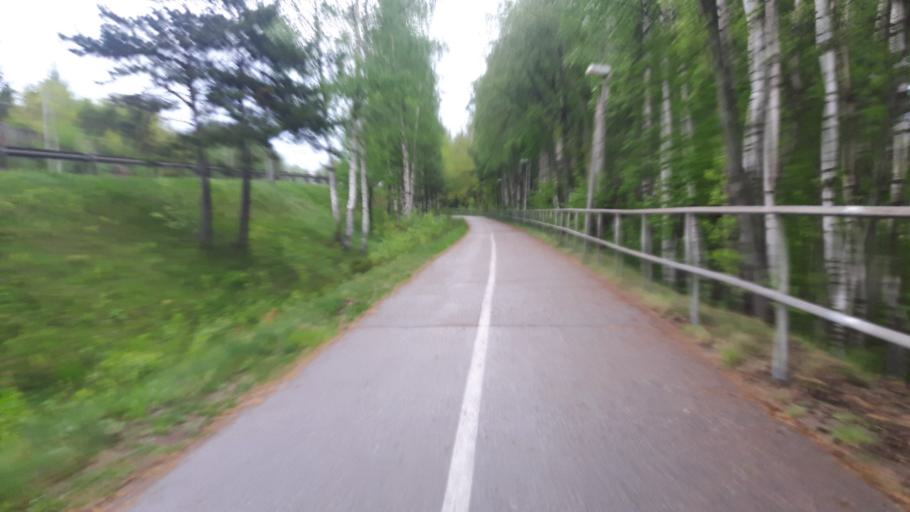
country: FI
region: Kymenlaakso
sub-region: Kotka-Hamina
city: Kotka
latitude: 60.4741
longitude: 26.9182
